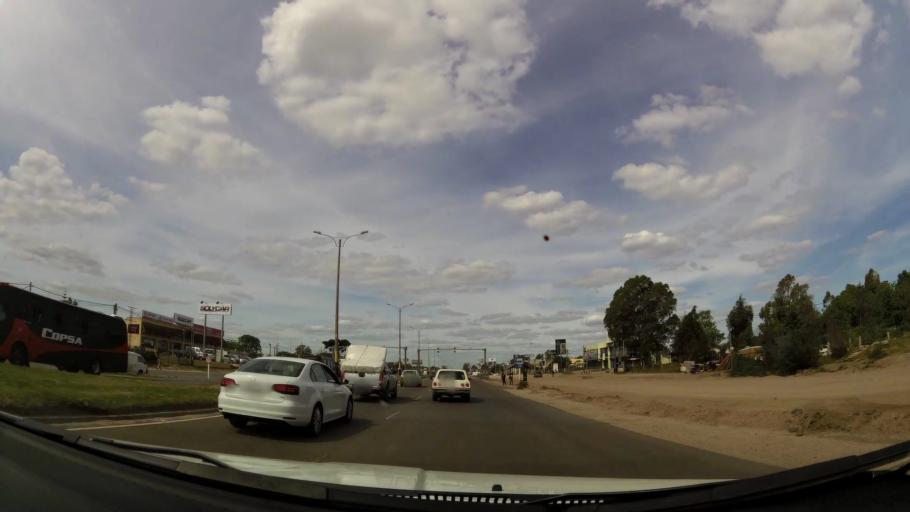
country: UY
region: Canelones
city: Barra de Carrasco
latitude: -34.8318
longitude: -55.9763
